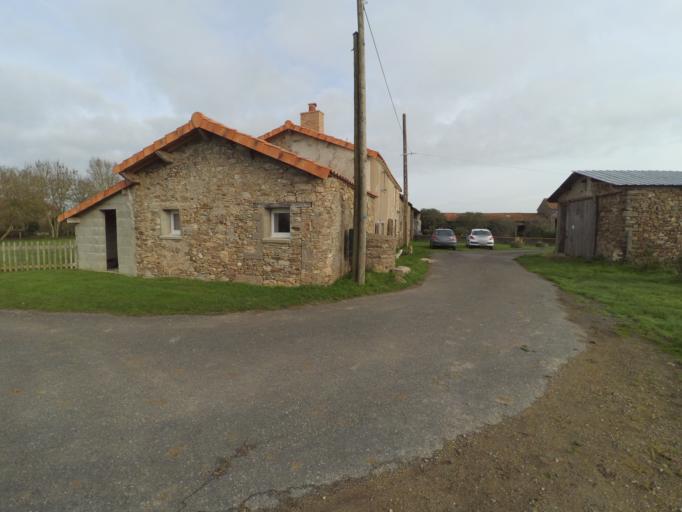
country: FR
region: Pays de la Loire
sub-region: Departement de la Loire-Atlantique
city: La Planche
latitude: 47.0048
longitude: -1.3889
